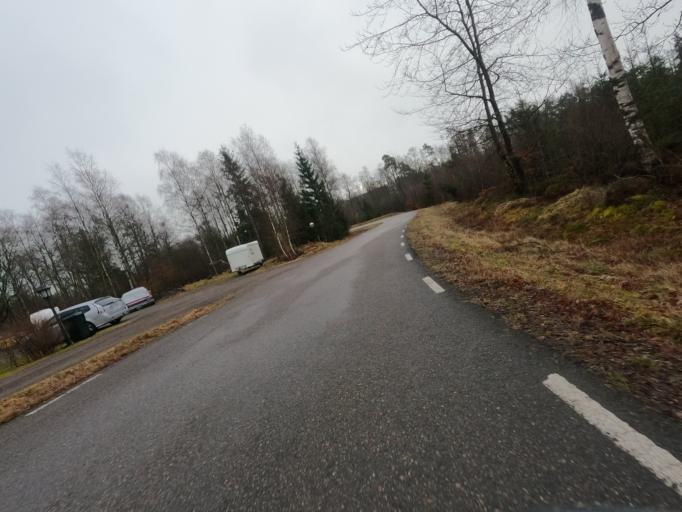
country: SE
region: Halland
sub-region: Hylte Kommun
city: Hyltebruk
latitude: 56.8272
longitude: 13.4264
